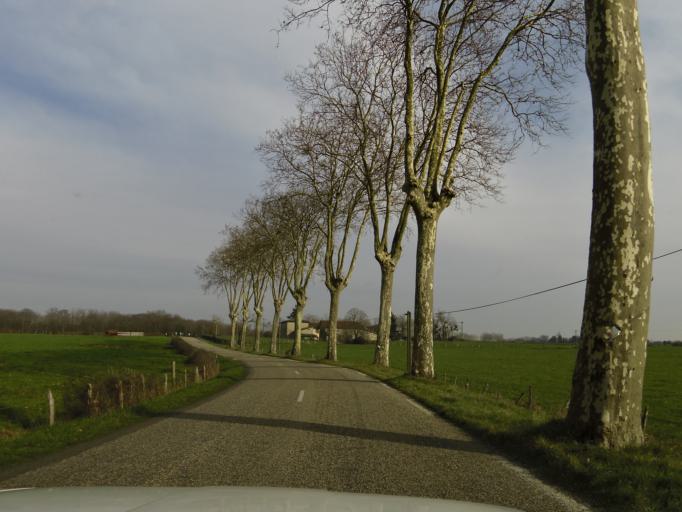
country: FR
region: Rhone-Alpes
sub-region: Departement de l'Ain
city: Chalamont
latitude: 46.0101
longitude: 5.1528
